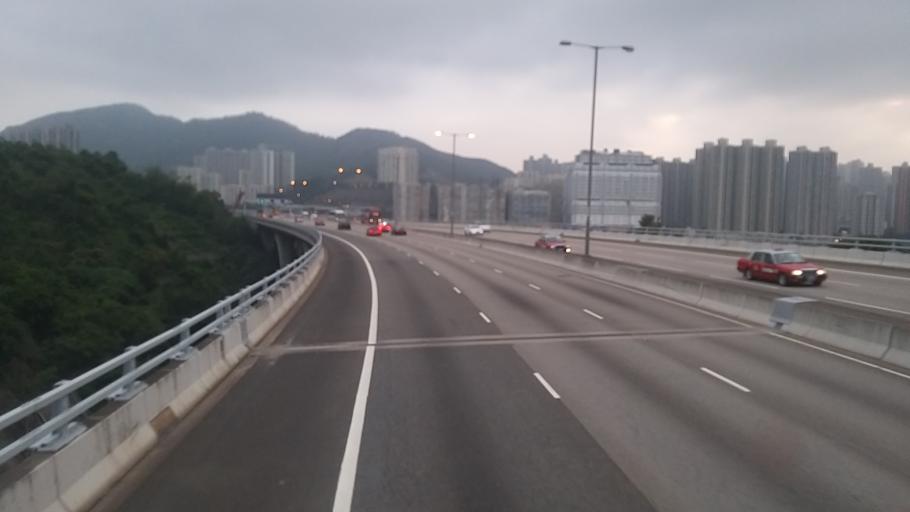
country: HK
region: Tsuen Wan
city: Tsuen Wan
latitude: 22.3521
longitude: 114.1188
